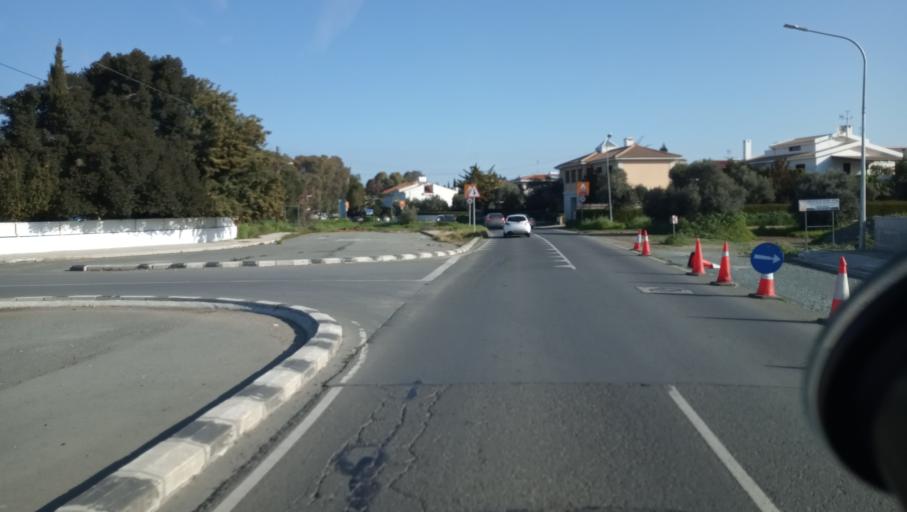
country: CY
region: Lefkosia
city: Nicosia
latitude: 35.1368
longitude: 33.3287
